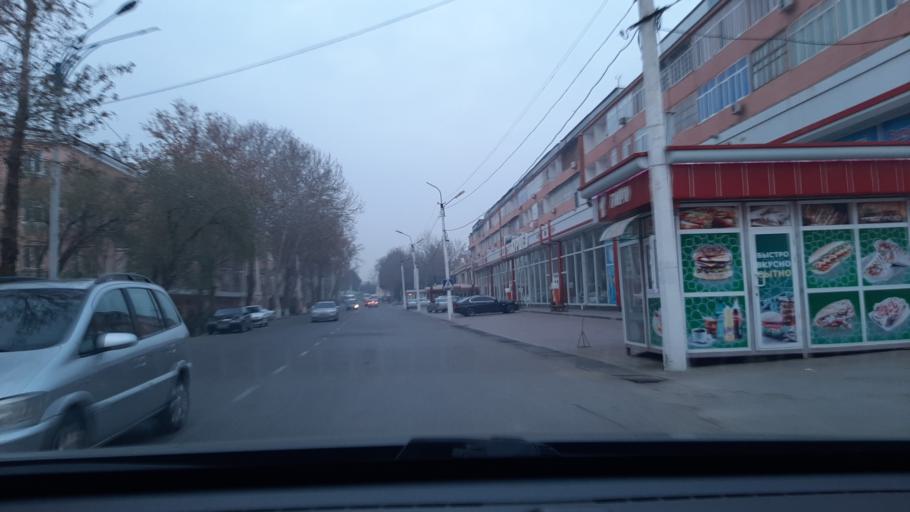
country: TJ
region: Viloyati Sughd
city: Khujand
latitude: 40.2716
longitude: 69.6048
